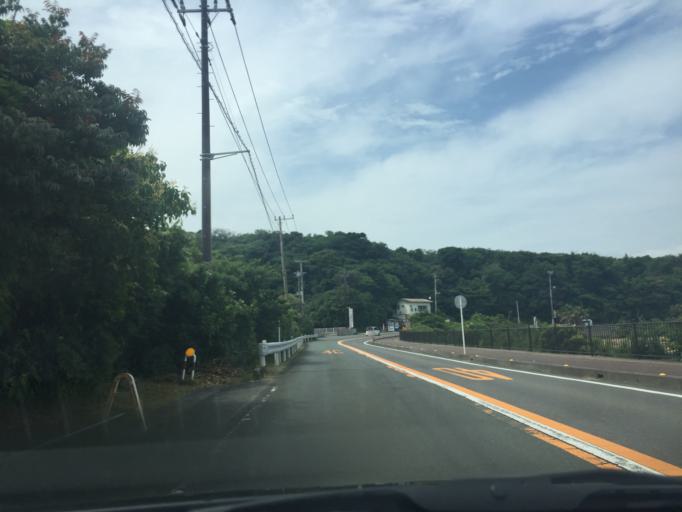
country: JP
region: Shizuoka
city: Shimoda
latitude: 34.6786
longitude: 138.9762
